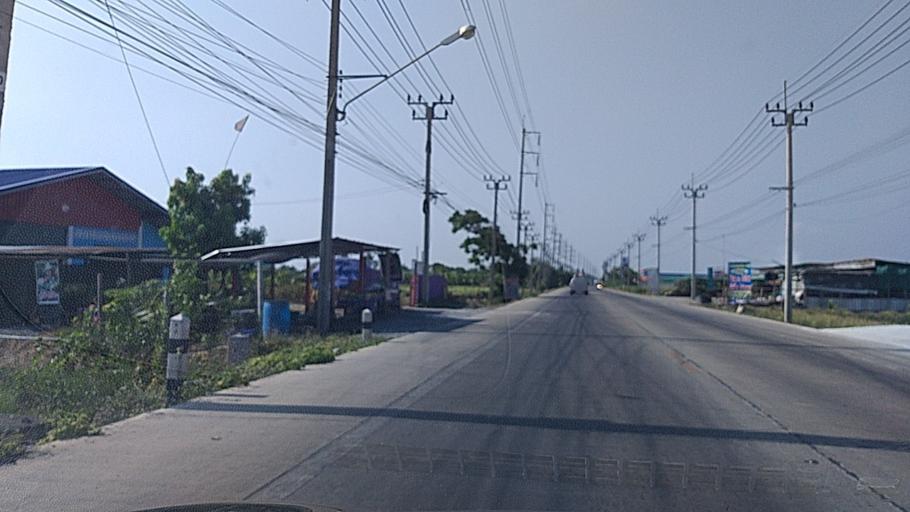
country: TH
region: Nonthaburi
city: Bang Yai
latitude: 13.9003
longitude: 100.3248
